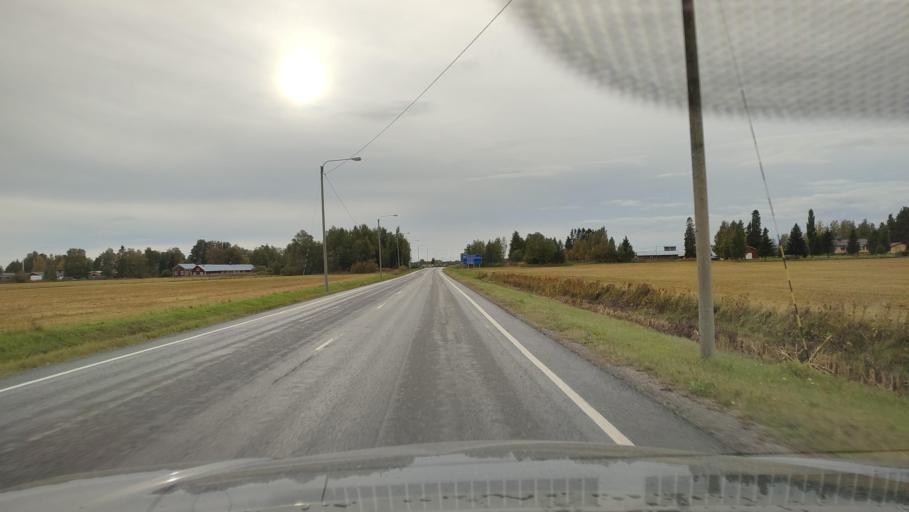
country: FI
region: Ostrobothnia
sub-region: Sydosterbotten
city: Kristinestad
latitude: 62.2614
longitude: 21.5149
